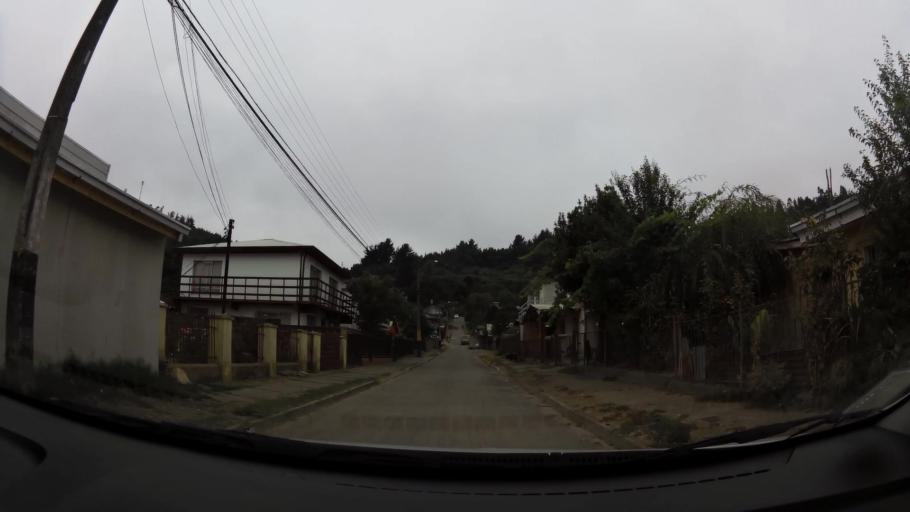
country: CL
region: Biobio
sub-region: Provincia de Concepcion
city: Concepcion
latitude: -36.8331
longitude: -72.9998
